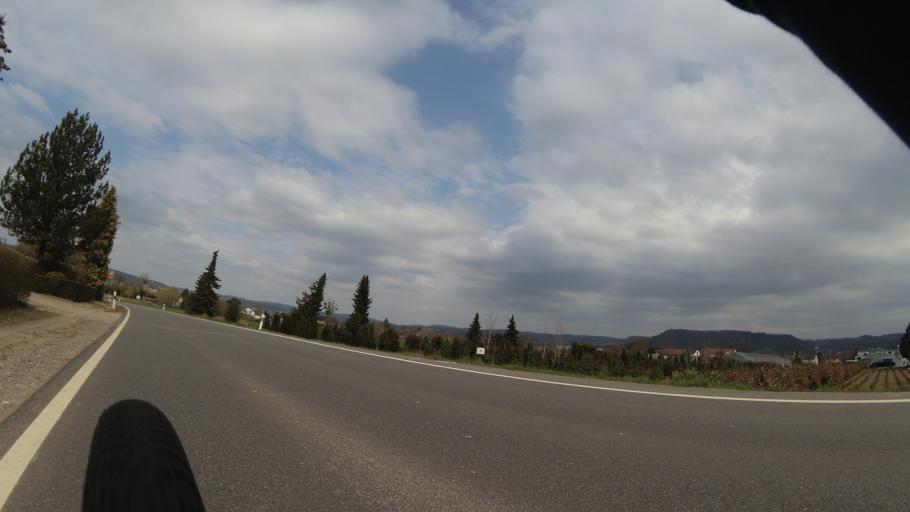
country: DE
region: Saarland
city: Merzig
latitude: 49.4440
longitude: 6.6095
